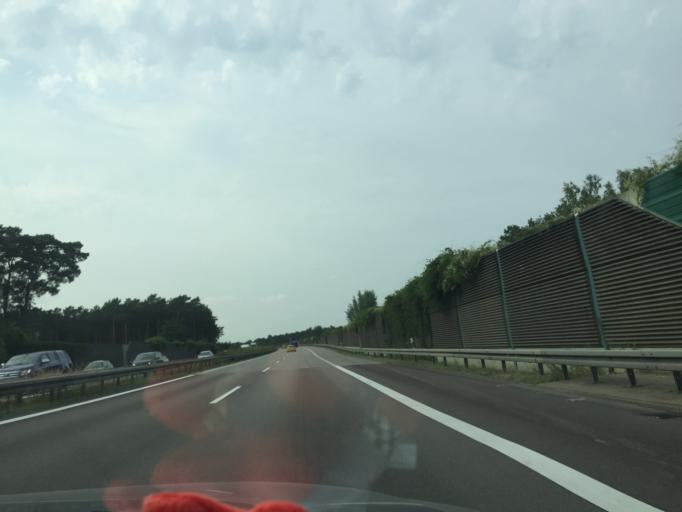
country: DE
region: Brandenburg
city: Schwerin
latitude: 52.1625
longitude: 13.6443
